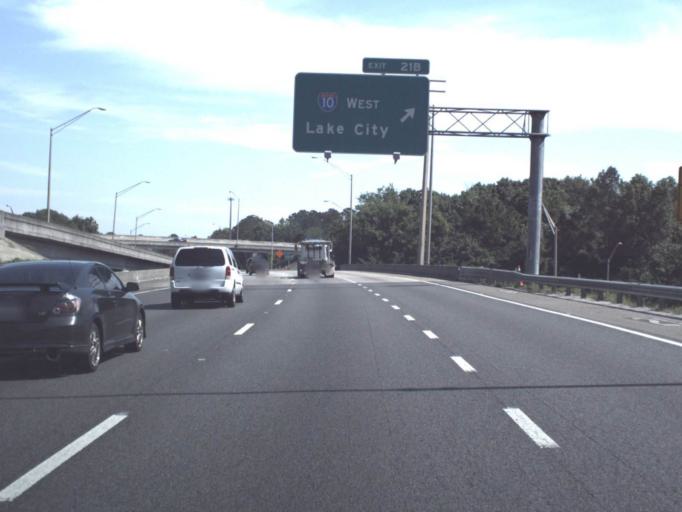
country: US
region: Florida
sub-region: Duval County
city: Jacksonville
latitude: 30.3144
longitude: -81.7691
